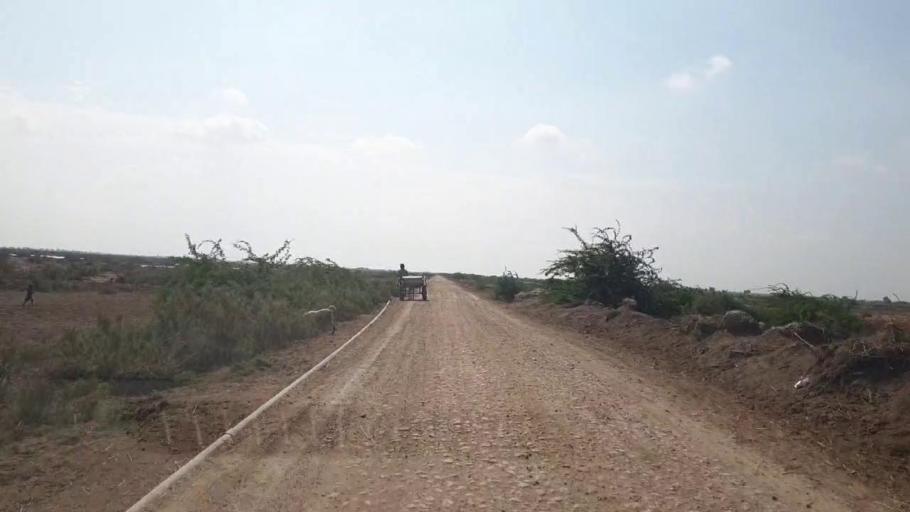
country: PK
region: Sindh
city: Badin
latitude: 24.5100
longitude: 68.6081
